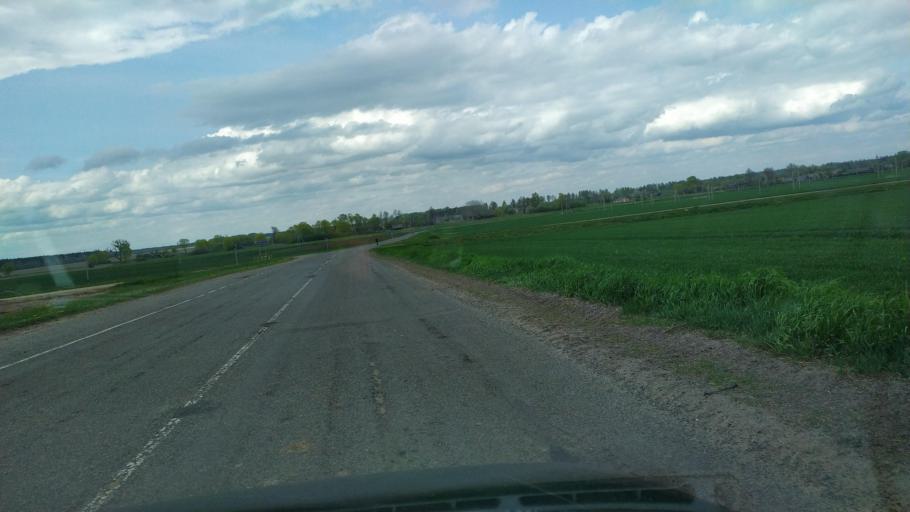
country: BY
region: Brest
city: Pruzhany
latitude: 52.6469
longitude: 24.3808
